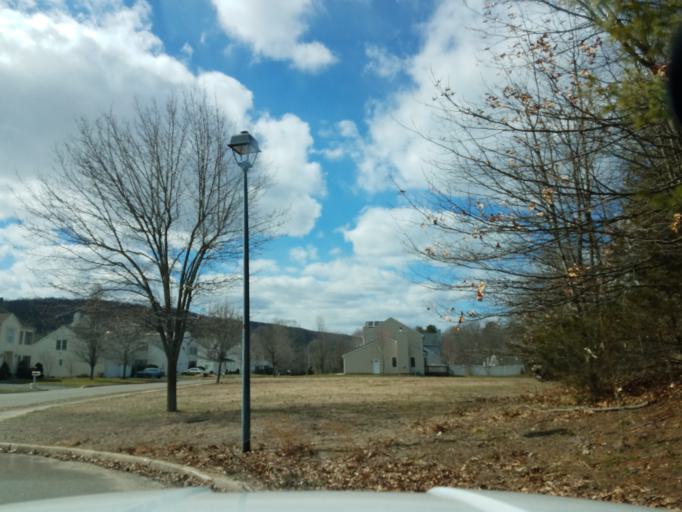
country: US
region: Connecticut
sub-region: New Haven County
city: Naugatuck
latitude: 41.4698
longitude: -73.0441
